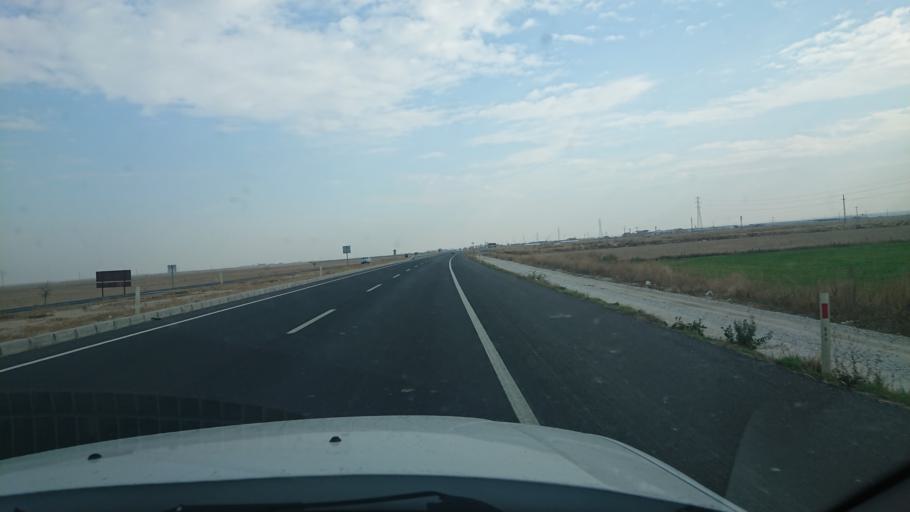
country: TR
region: Aksaray
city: Yesilova
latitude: 38.2991
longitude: 33.7909
